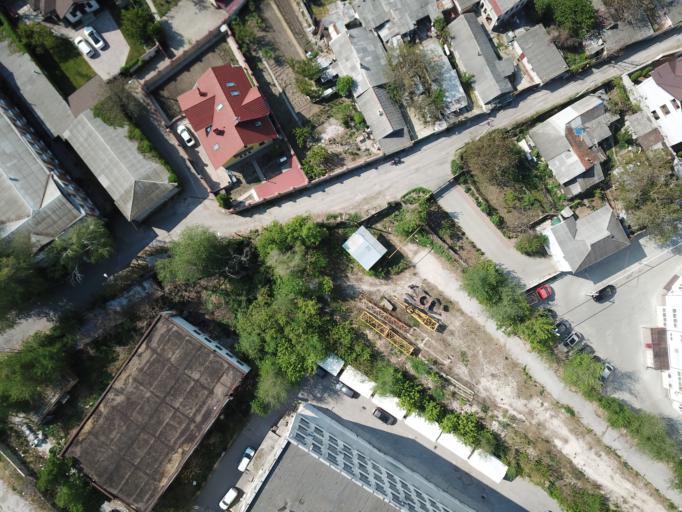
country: MD
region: Chisinau
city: Chisinau
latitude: 47.0100
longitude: 28.8543
